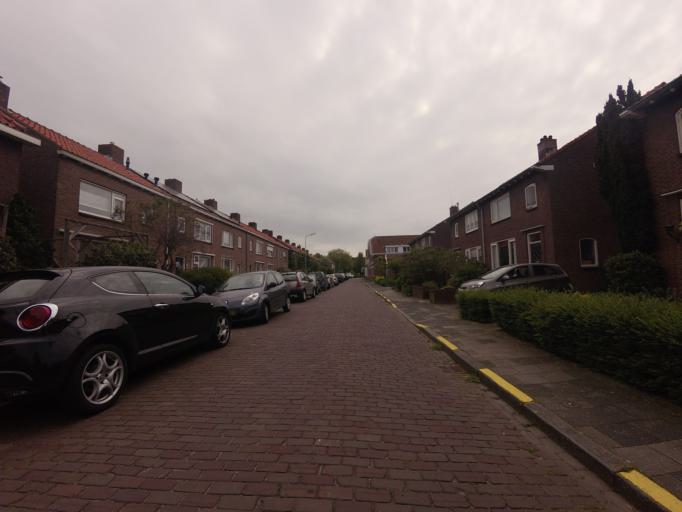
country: NL
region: Zeeland
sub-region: Gemeente Middelburg
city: Middelburg
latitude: 51.5022
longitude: 3.6028
